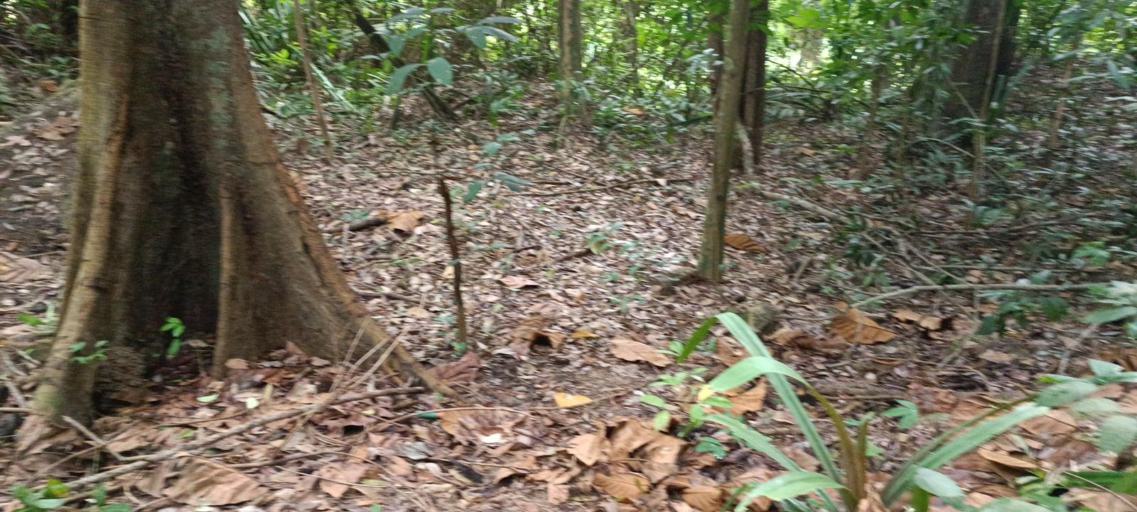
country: MY
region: Penang
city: George Town
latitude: 5.3875
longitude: 100.2936
